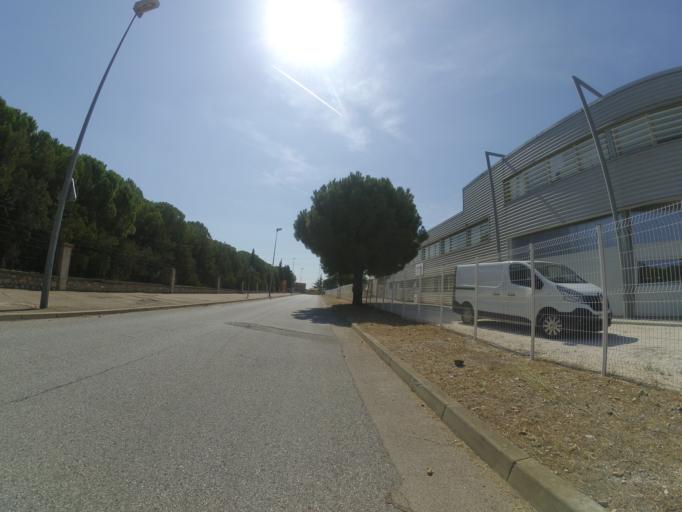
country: FR
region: Languedoc-Roussillon
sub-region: Departement des Pyrenees-Orientales
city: Salses-le-Chateau
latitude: 42.8032
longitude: 2.8937
